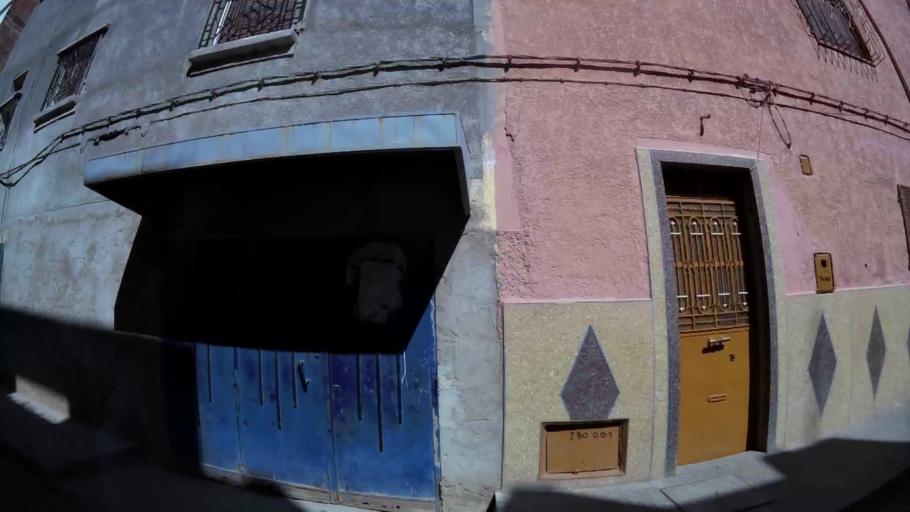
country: MA
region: Oriental
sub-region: Oujda-Angad
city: Oujda
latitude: 34.6911
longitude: -1.9270
